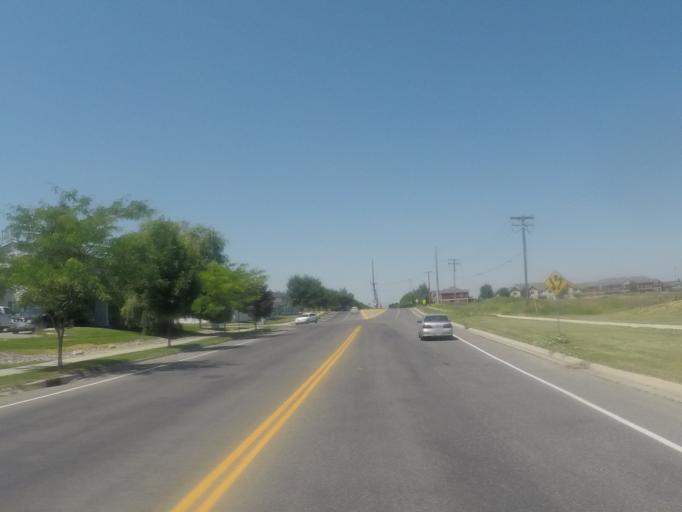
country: US
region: Montana
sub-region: Gallatin County
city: Bozeman
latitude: 45.6930
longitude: -111.0697
